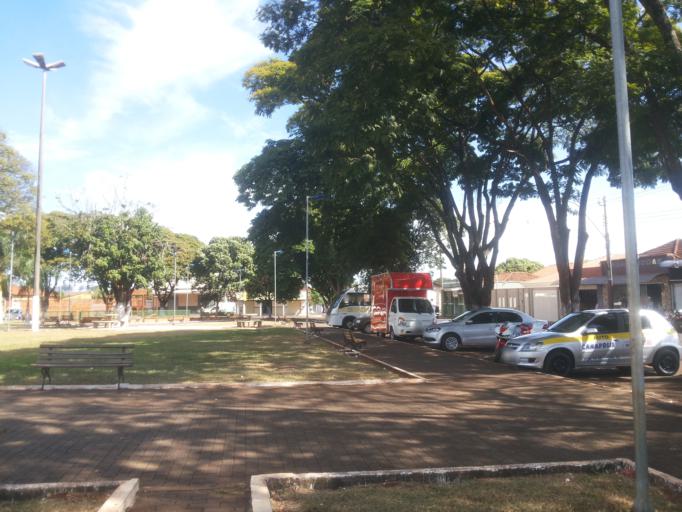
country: BR
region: Minas Gerais
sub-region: Centralina
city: Centralina
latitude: -18.7248
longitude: -49.2054
